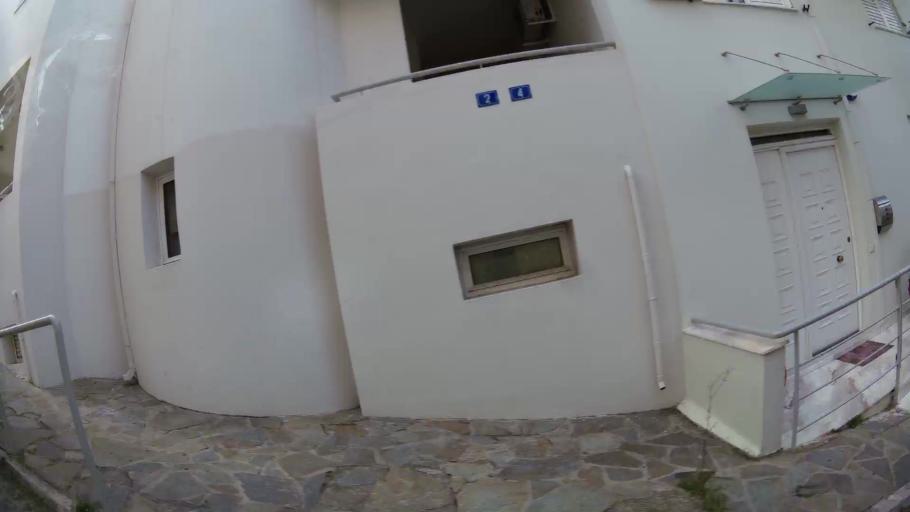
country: GR
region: Attica
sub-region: Nomarchia Athinas
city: Kipseli
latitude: 37.9953
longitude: 23.7578
